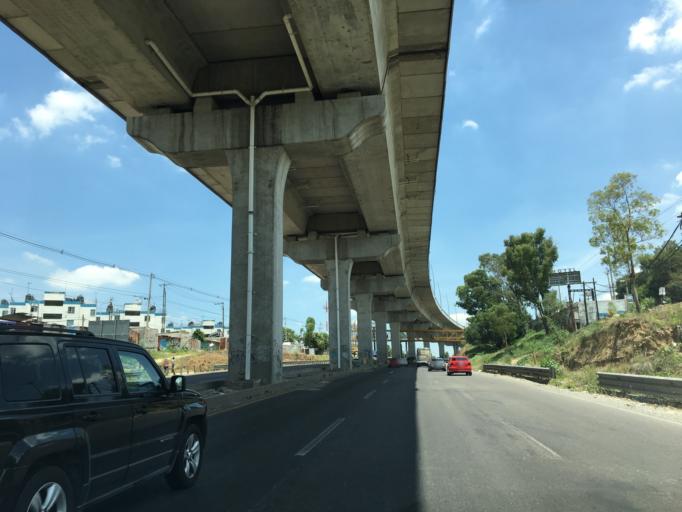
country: MX
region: Puebla
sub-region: Cuautlancingo
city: Sanctorum
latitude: 19.1016
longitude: -98.2375
